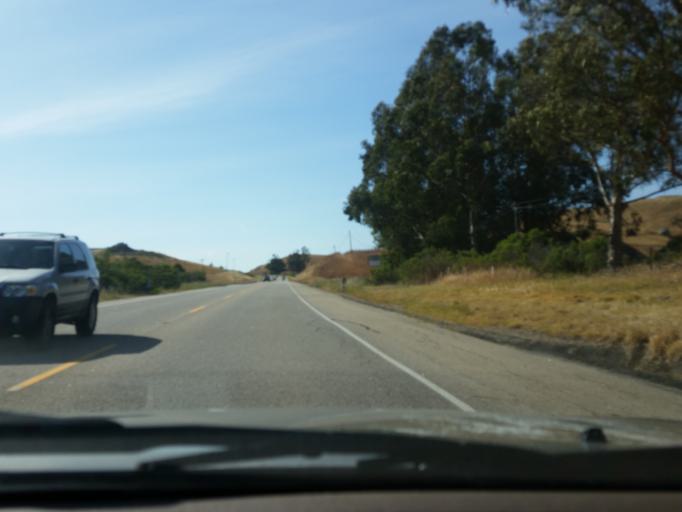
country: US
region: California
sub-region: San Luis Obispo County
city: Cambria
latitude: 35.4985
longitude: -121.0100
